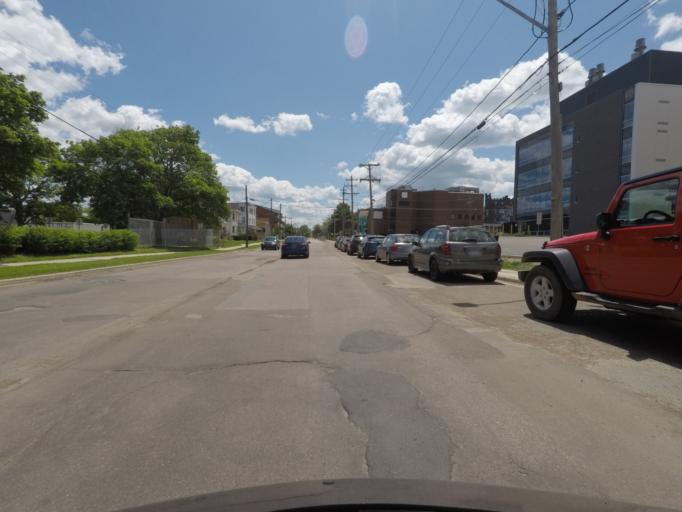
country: CA
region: New Brunswick
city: Moncton
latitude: 46.0975
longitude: -64.7858
